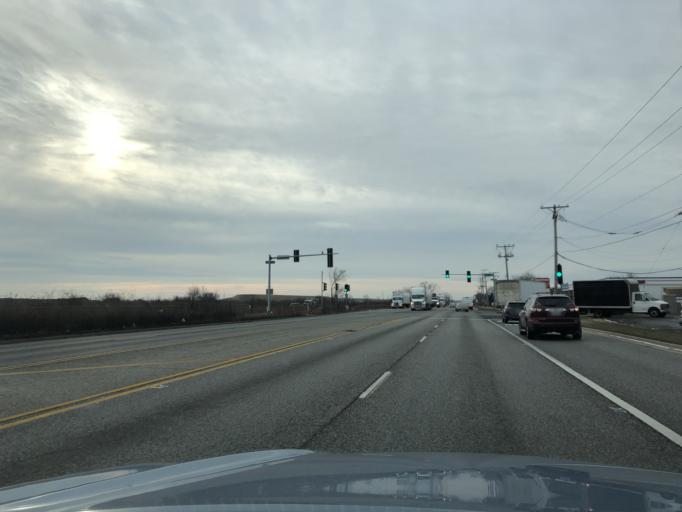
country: US
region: Illinois
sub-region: Cook County
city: Elk Grove Village
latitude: 41.9943
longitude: -87.9401
